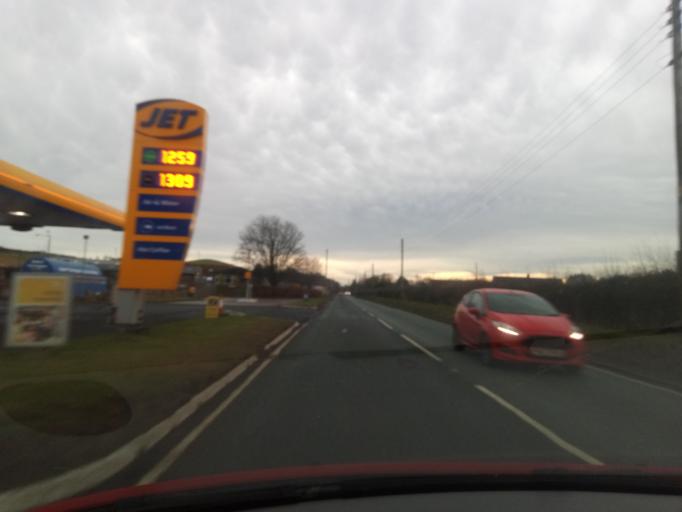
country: GB
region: England
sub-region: Northumberland
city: Wooler
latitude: 55.5314
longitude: -1.9996
